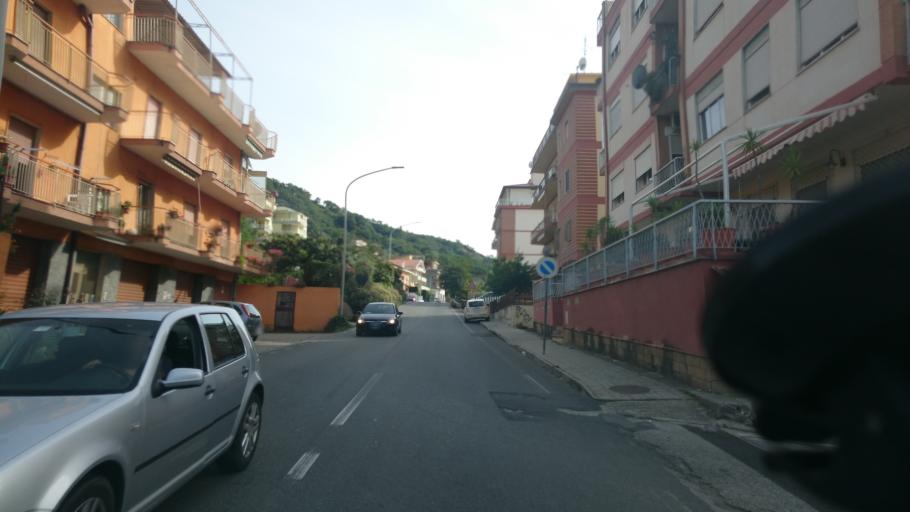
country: IT
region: Calabria
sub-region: Provincia di Vibo-Valentia
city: Sant'Onofrio
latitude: 38.7137
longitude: 16.1280
